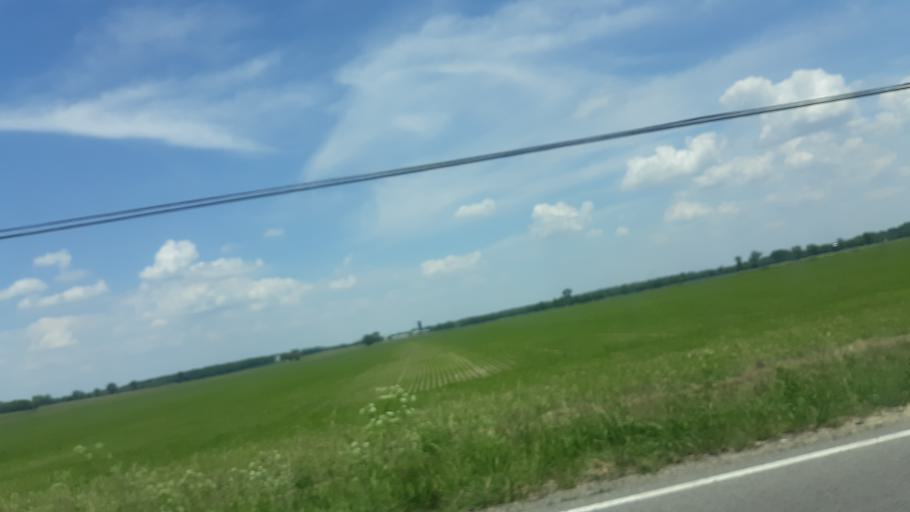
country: US
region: Illinois
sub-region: Saline County
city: Harrisburg
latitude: 37.6364
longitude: -88.4976
